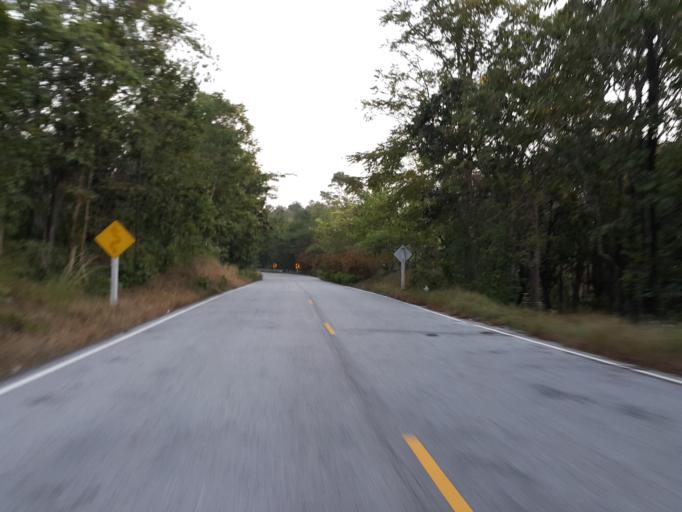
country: TH
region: Lampang
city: Thoen
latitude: 17.6602
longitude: 99.1175
